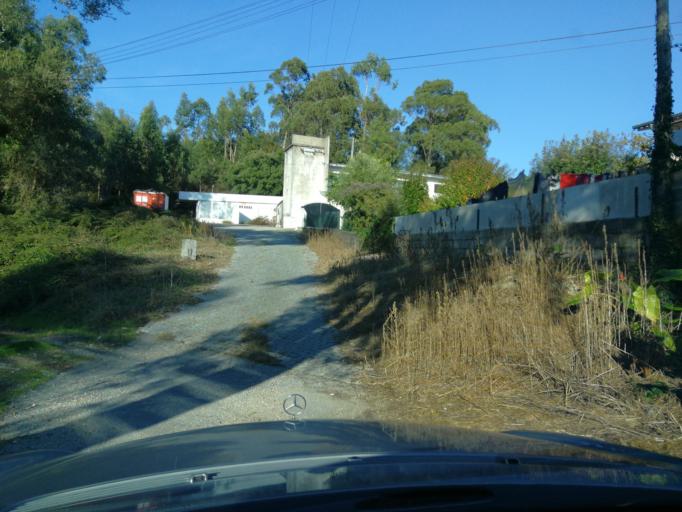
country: PT
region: Braga
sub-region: Vila Nova de Famalicao
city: Vila Nova de Famalicao
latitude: 41.4313
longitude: -8.5145
